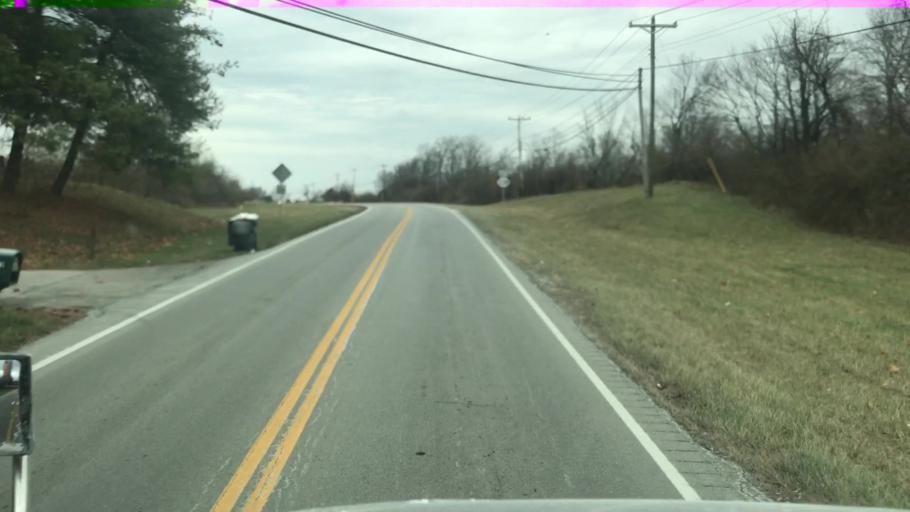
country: US
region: Kentucky
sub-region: Boone County
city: Walton
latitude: 38.9156
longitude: -84.6223
